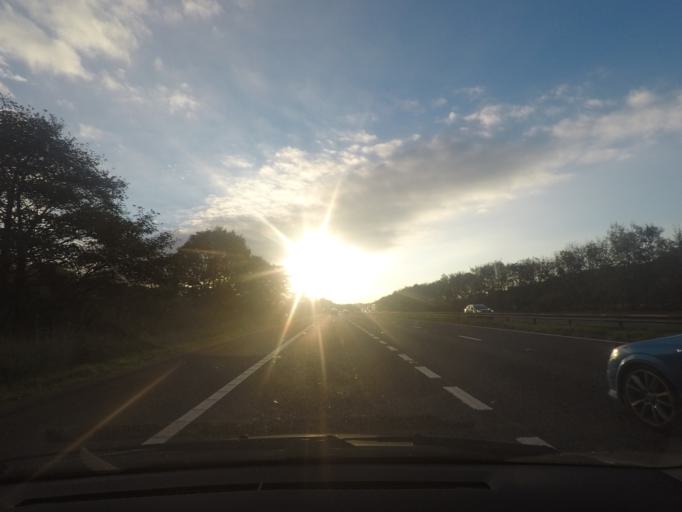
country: GB
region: England
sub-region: North Lincolnshire
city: Scawby
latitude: 53.5469
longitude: -0.5369
